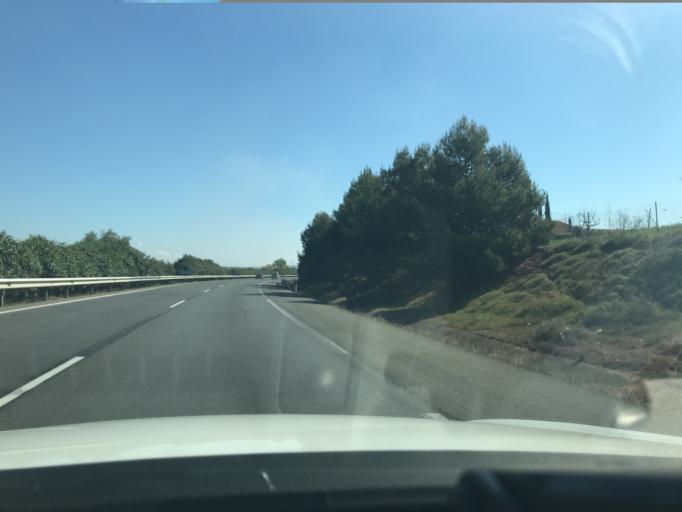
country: ES
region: Andalusia
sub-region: Province of Cordoba
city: Villafranca de Cordoba
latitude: 37.9508
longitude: -4.5374
